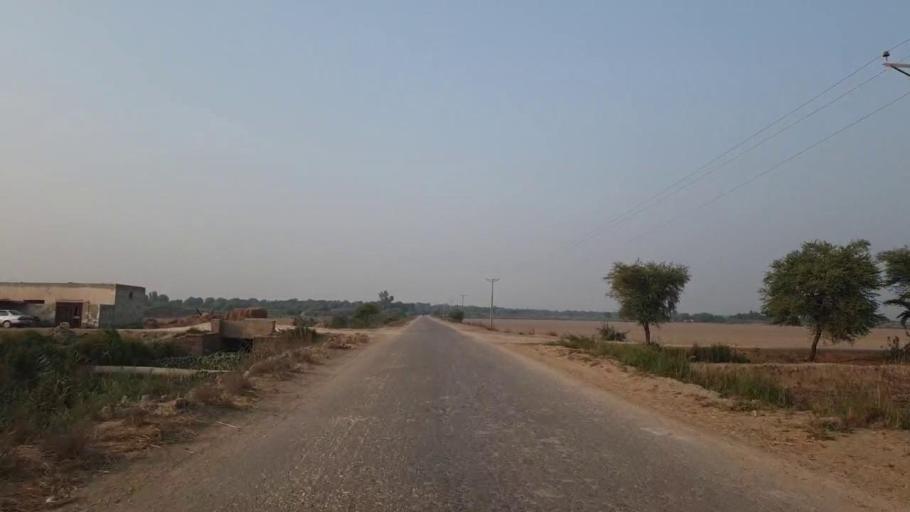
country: PK
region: Sindh
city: Tando Muhammad Khan
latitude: 25.1100
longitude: 68.4292
